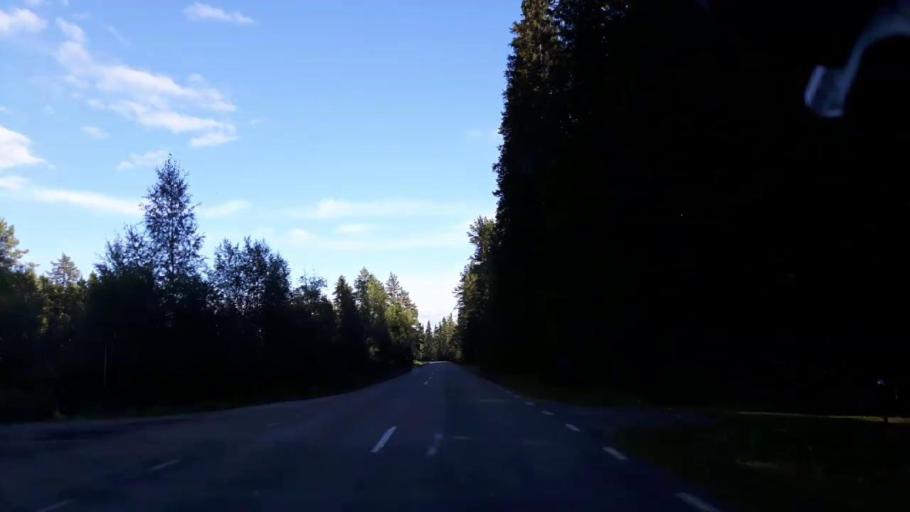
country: SE
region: Jaemtland
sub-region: Stroemsunds Kommun
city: Stroemsund
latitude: 63.3892
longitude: 15.5666
